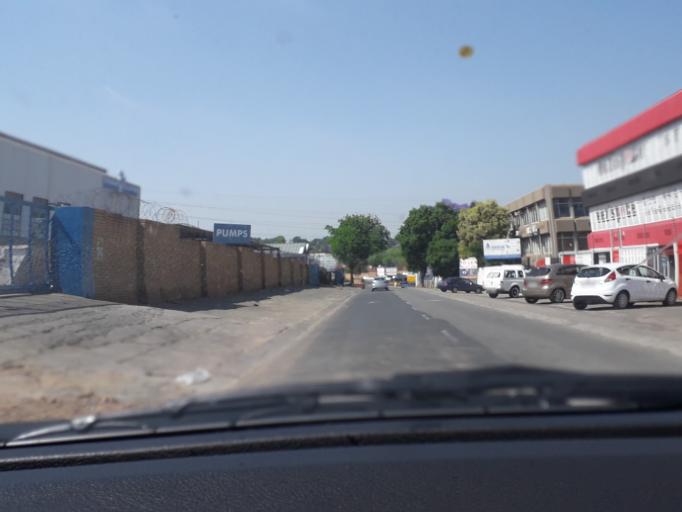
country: ZA
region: Gauteng
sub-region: City of Johannesburg Metropolitan Municipality
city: Modderfontein
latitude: -26.1137
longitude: 28.0810
